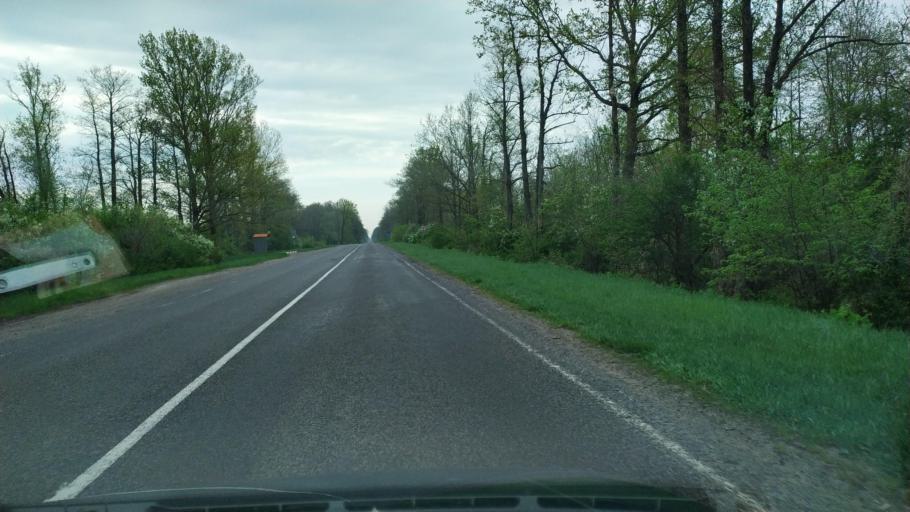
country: BY
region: Brest
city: Zhabinka
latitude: 52.2884
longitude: 23.9427
